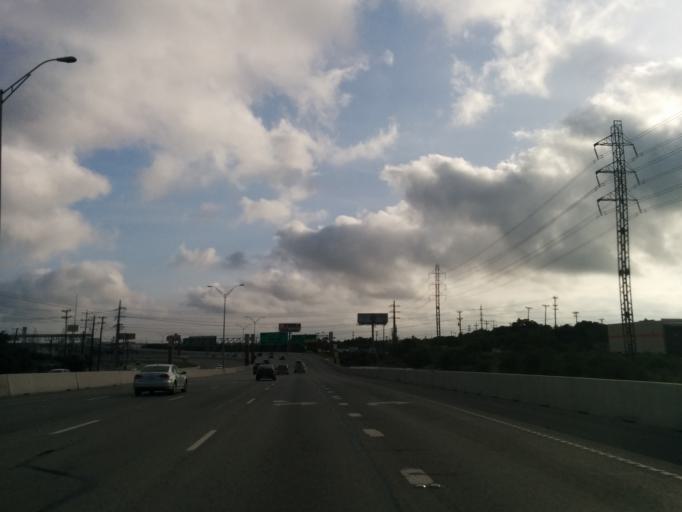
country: US
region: Texas
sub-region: Bexar County
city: Alamo Heights
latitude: 29.5084
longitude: -98.4774
